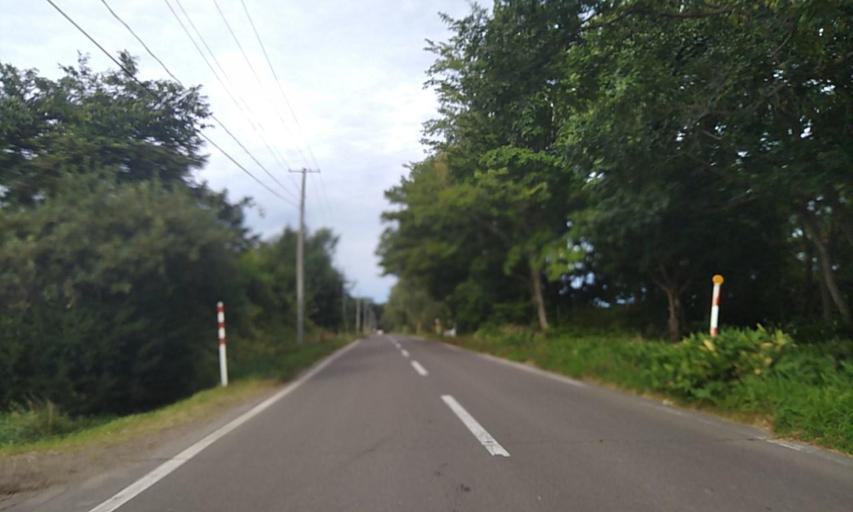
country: JP
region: Hokkaido
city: Abashiri
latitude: 43.7954
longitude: 144.5557
